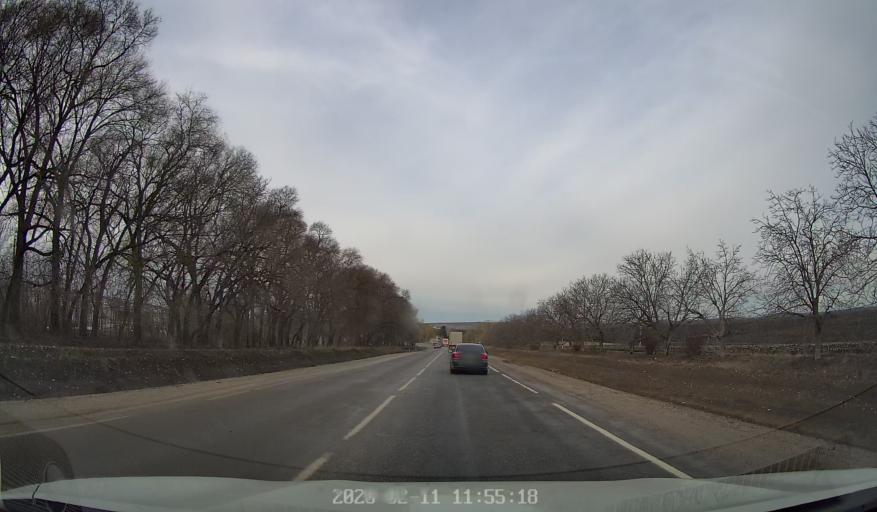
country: MD
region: Riscani
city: Riscani
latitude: 47.8880
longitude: 27.6954
